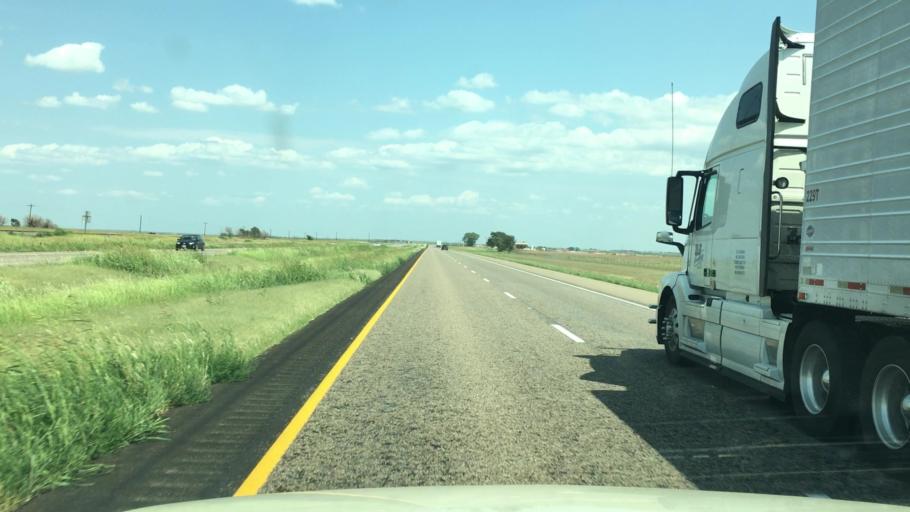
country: US
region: Texas
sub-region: Armstrong County
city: Claude
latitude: 35.0318
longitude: -101.1254
